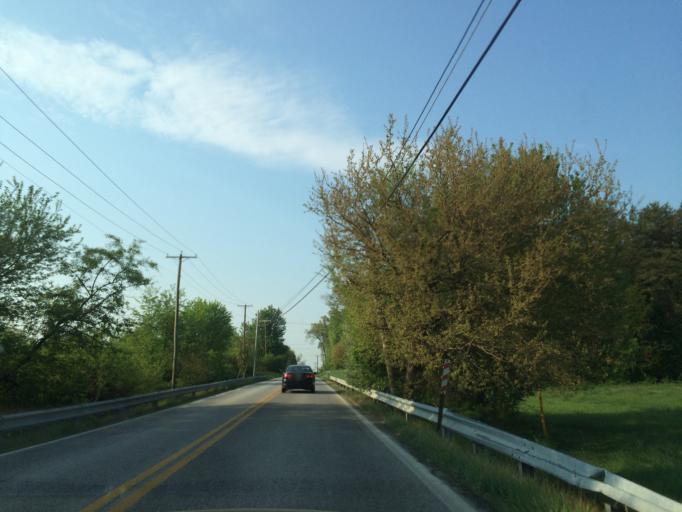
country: US
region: Maryland
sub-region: Howard County
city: Highland
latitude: 39.2553
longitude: -76.9835
